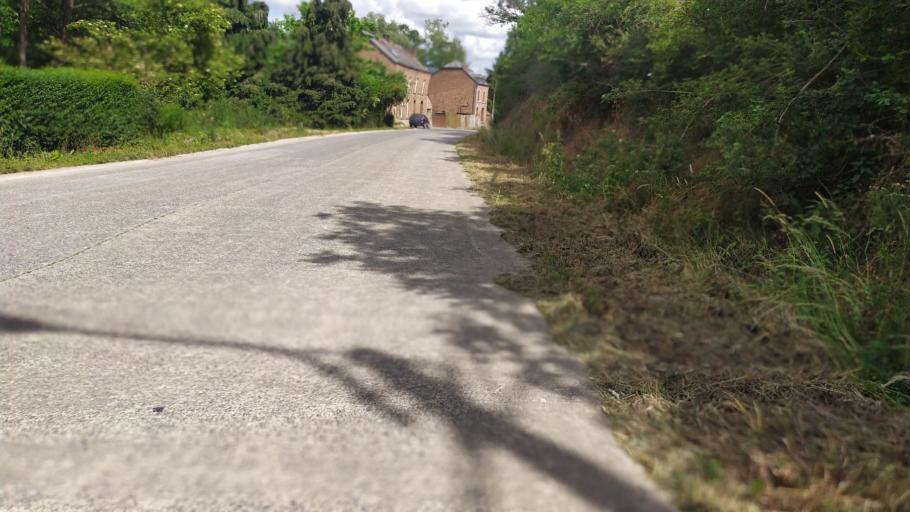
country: BE
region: Wallonia
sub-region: Province de Namur
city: Houyet
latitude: 50.1686
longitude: 5.0463
